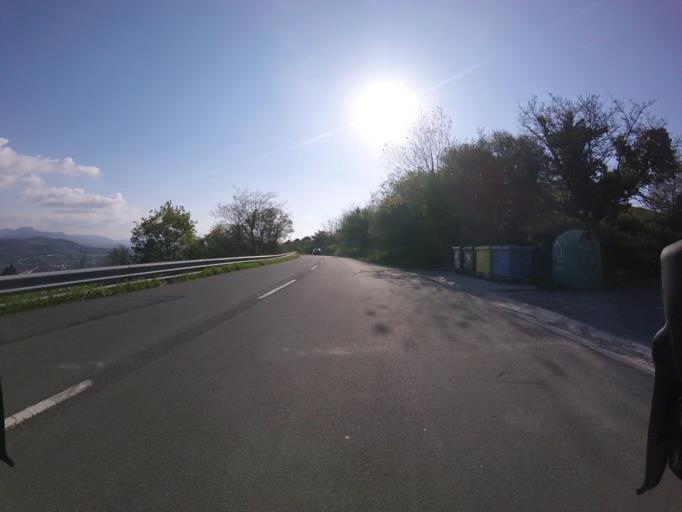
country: ES
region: Basque Country
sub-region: Provincia de Guipuzcoa
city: Lezo
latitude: 43.3338
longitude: -1.8979
